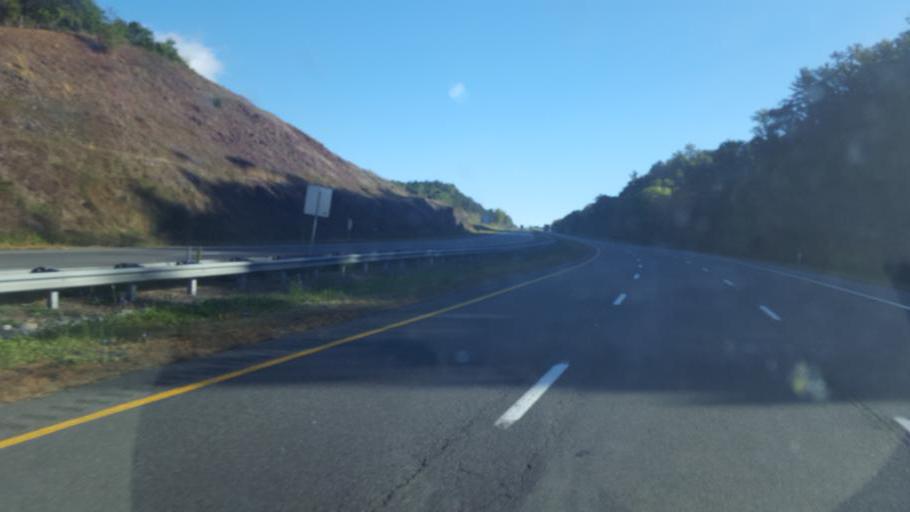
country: US
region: West Virginia
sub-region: Morgan County
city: Berkeley Springs
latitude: 39.7039
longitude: -78.3130
